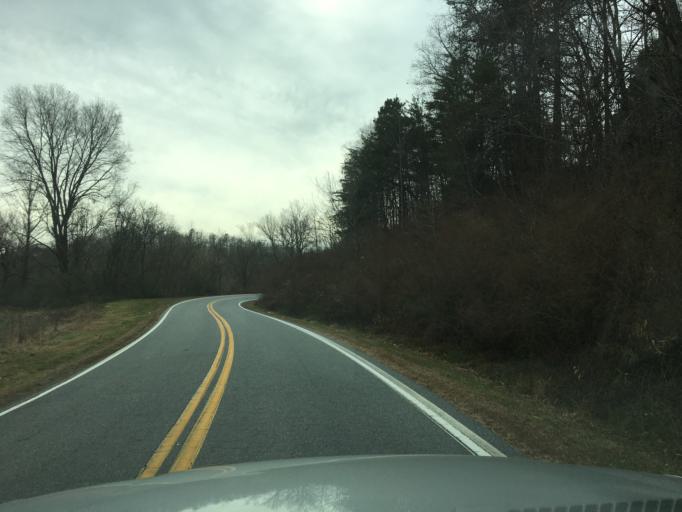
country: US
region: North Carolina
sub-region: McDowell County
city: West Marion
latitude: 35.6213
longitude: -81.9686
